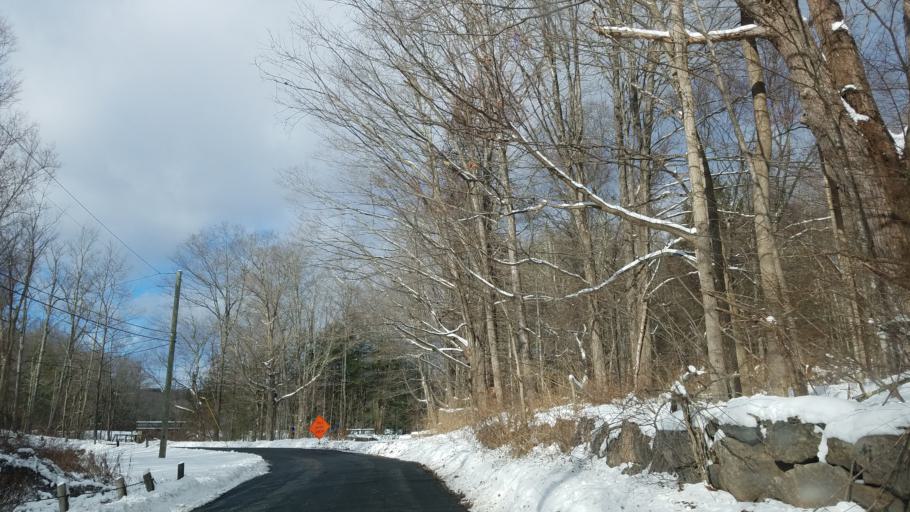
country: US
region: Connecticut
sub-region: Litchfield County
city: Winsted
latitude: 41.9677
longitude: -73.0584
